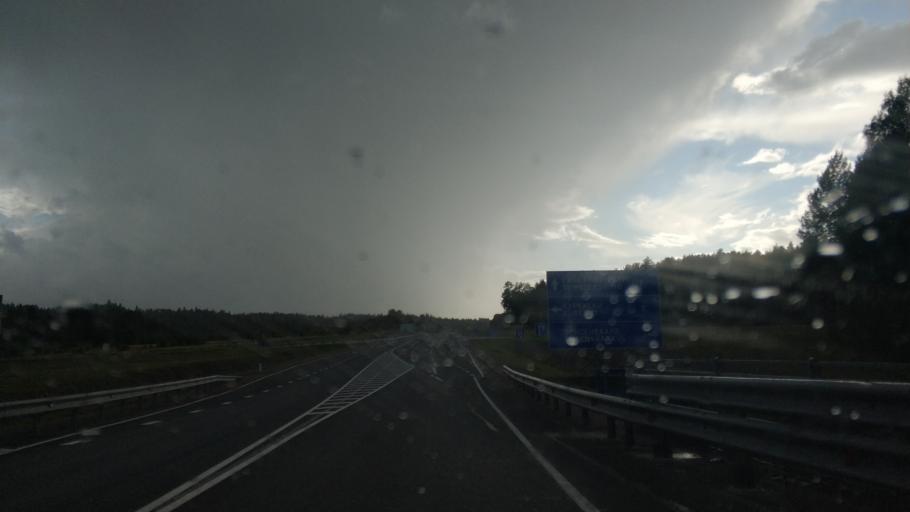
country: RU
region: Leningrad
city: Kuznechnoye
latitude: 61.3403
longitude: 29.8625
